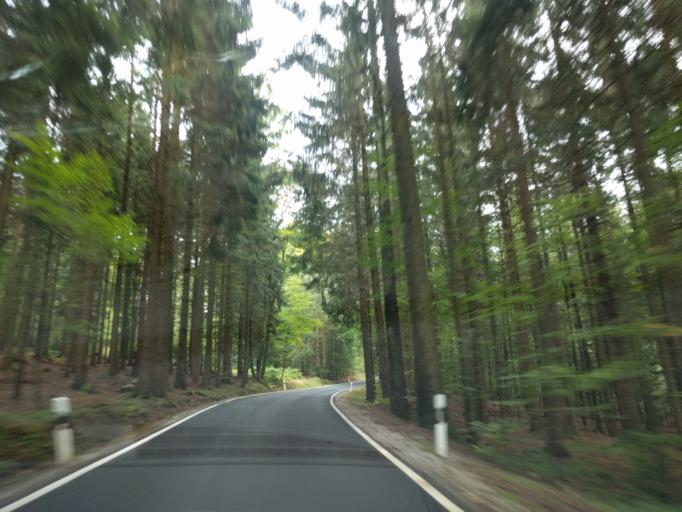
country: DE
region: Bavaria
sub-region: Lower Bavaria
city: Grafling
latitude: 48.8814
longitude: 13.0147
